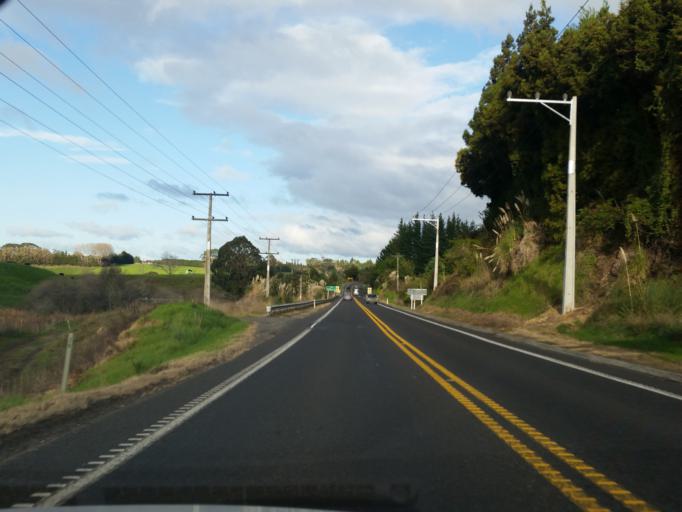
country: NZ
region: Bay of Plenty
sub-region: Tauranga City
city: Tauranga
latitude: -37.6664
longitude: 176.0169
